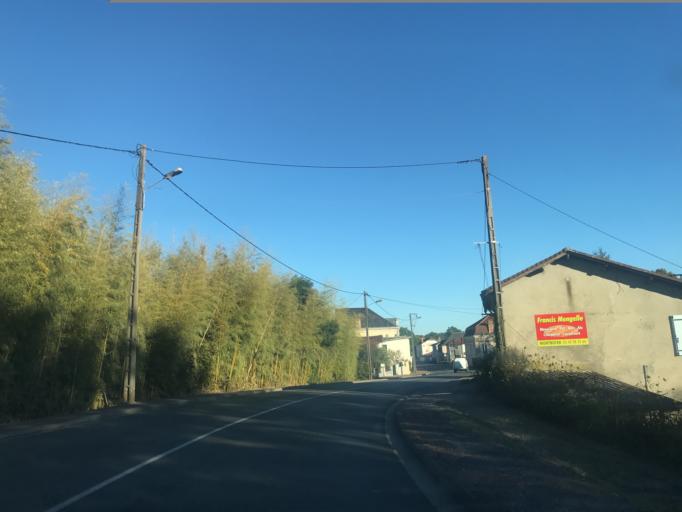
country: FR
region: Poitou-Charentes
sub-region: Departement de la Charente-Maritime
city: Saint-Aigulin
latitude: 45.1605
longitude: -0.0195
